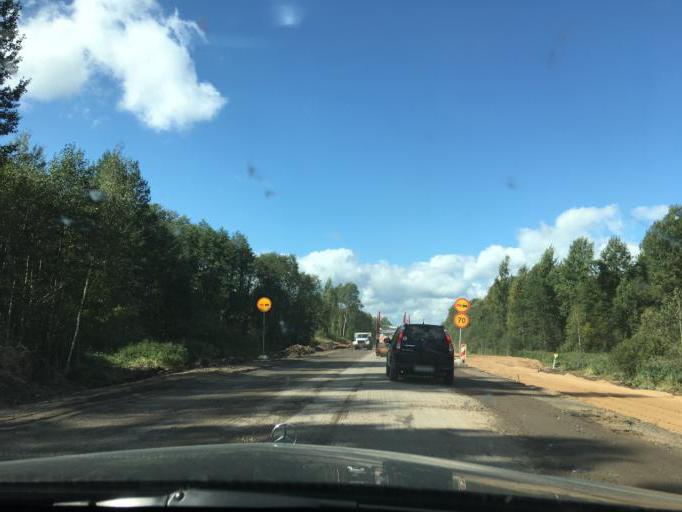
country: RU
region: Pskov
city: Novosokol'niki
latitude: 56.2723
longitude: 30.3489
